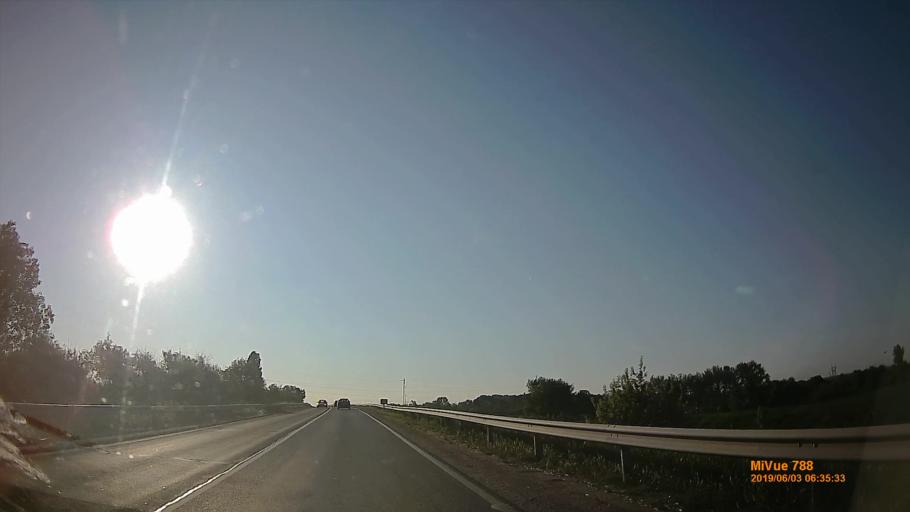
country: HU
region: Pest
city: Taksony
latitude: 47.3084
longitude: 19.0704
